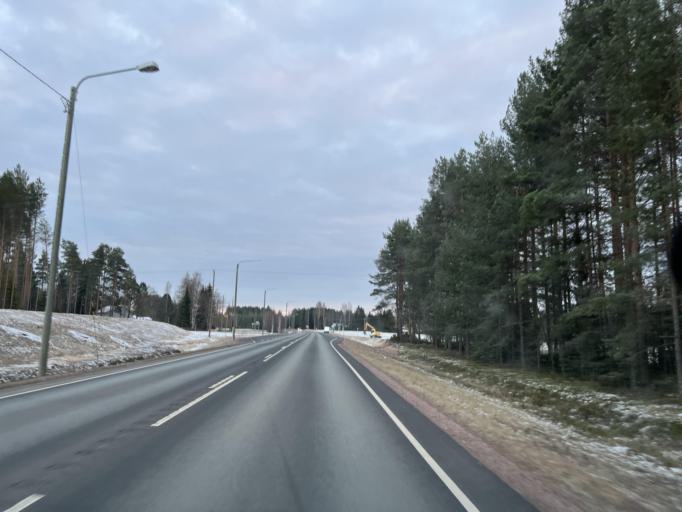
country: FI
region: Northern Ostrobothnia
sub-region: Oulu
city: Muhos
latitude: 64.8746
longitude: 25.8583
